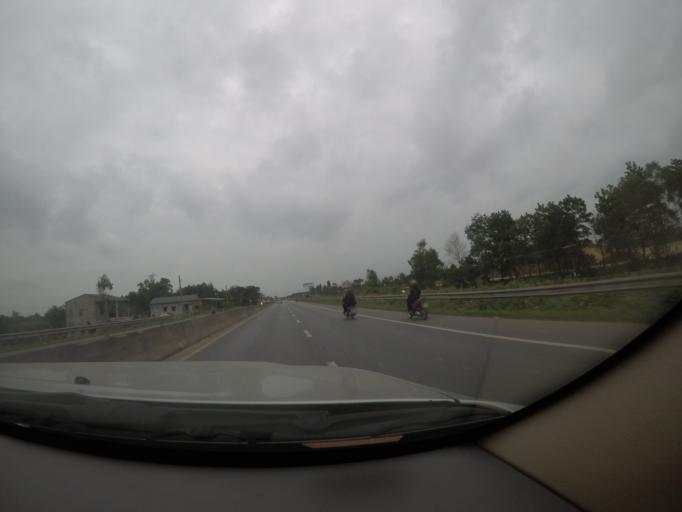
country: VN
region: Quang Tri
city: Hai Lang
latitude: 16.7031
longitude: 107.2248
